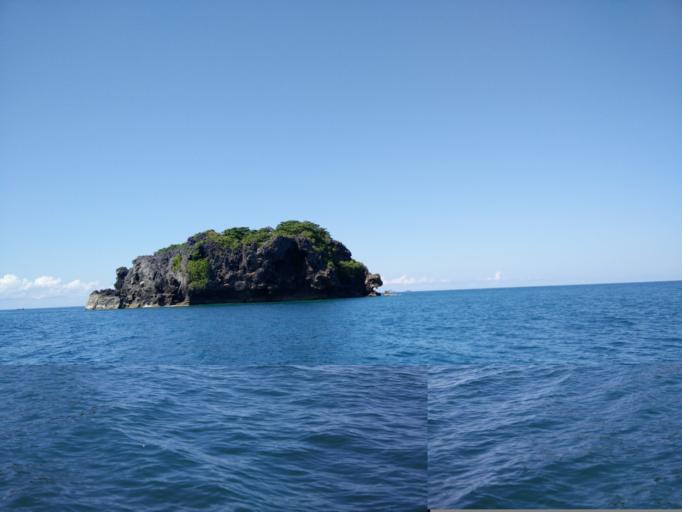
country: MM
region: Ayeyarwady
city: Pathein
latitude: 16.8519
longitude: 94.2725
